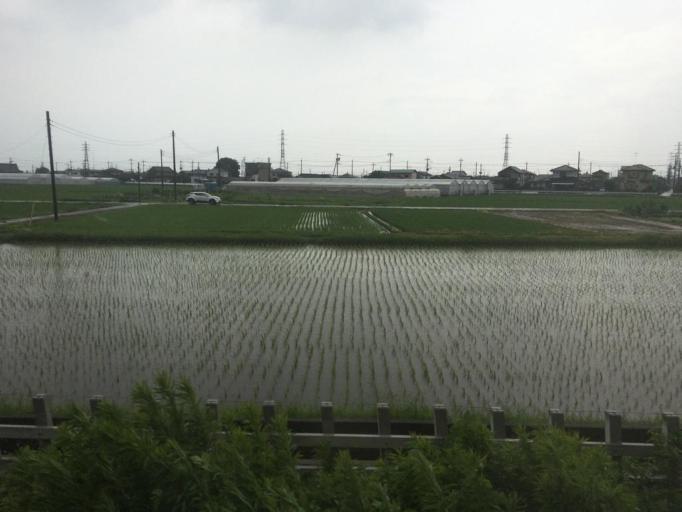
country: JP
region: Tochigi
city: Ashikaga
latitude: 36.2983
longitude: 139.4618
